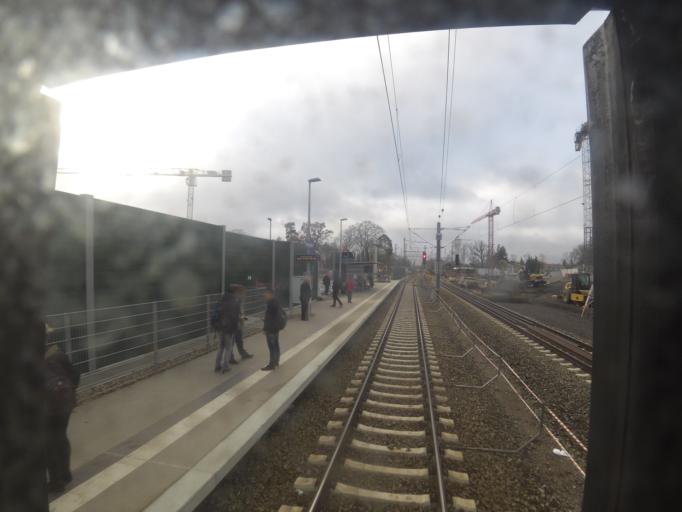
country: DE
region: Brandenburg
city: Rangsdorf
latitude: 52.2944
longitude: 13.4309
